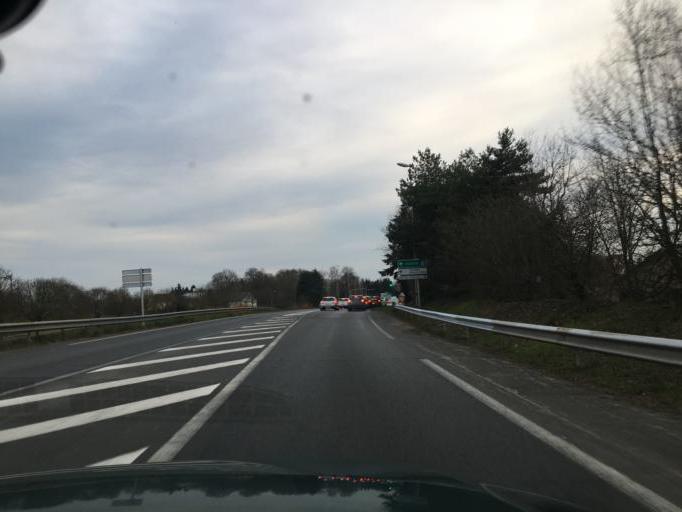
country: FR
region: Centre
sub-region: Departement du Loiret
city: Saint-Jean-le-Blanc
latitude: 47.8868
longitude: 1.9246
